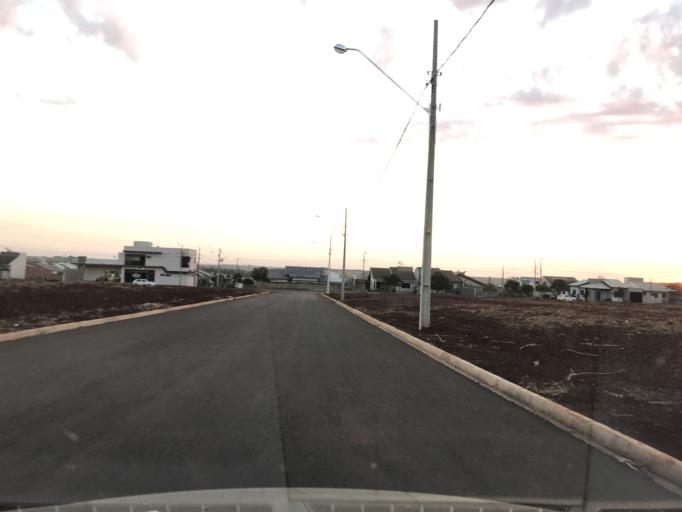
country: BR
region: Parana
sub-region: Palotina
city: Palotina
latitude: -24.3024
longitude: -53.8363
